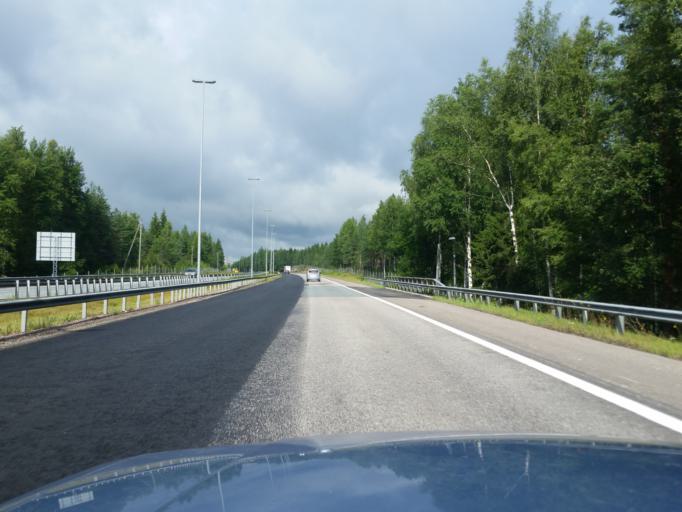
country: FI
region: Uusimaa
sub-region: Helsinki
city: Espoo
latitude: 60.2533
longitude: 24.5251
